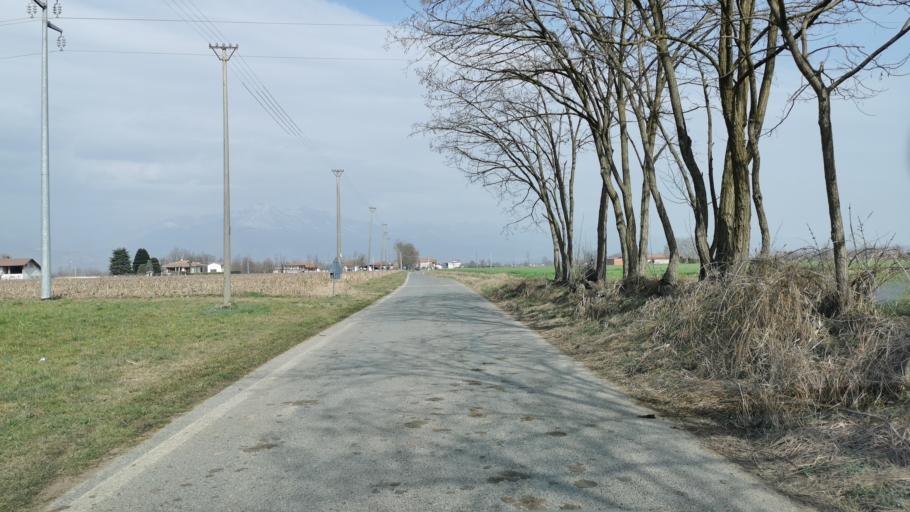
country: IT
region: Piedmont
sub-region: Provincia di Torino
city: Front
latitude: 45.2912
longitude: 7.6881
